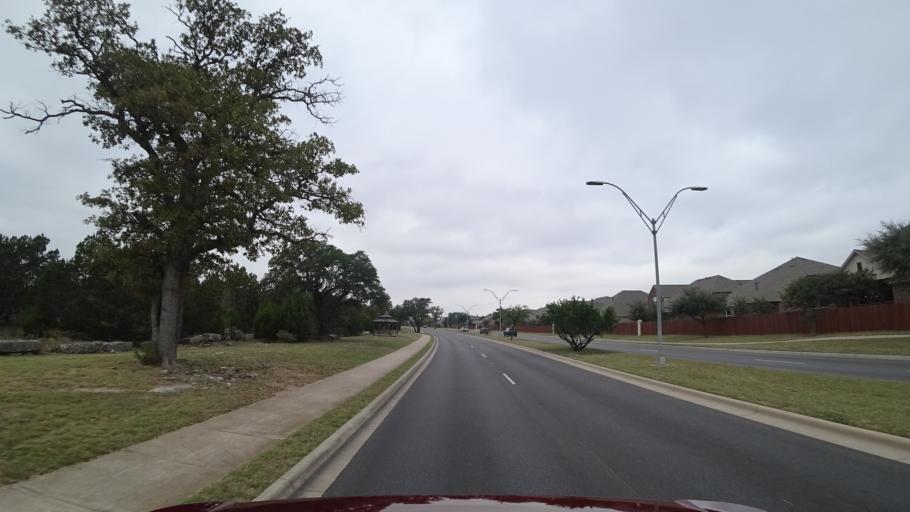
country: US
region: Texas
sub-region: Williamson County
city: Cedar Park
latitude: 30.4955
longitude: -97.8417
